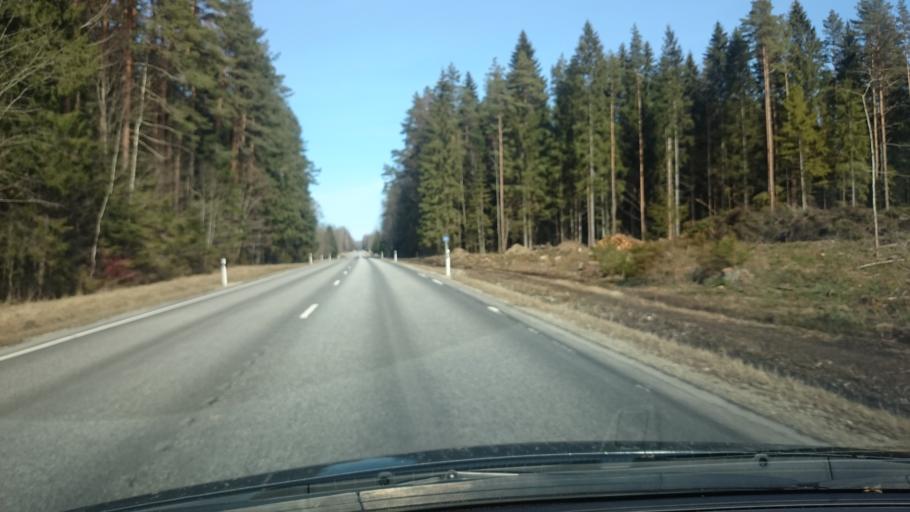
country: EE
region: Jaervamaa
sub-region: Tueri vald
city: Sarevere
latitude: 58.7019
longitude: 25.2613
